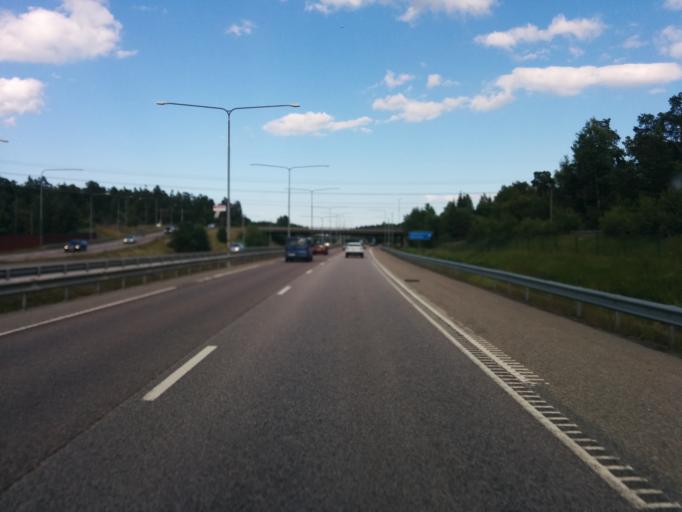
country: SE
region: Stockholm
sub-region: Nacka Kommun
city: Fisksatra
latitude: 59.3153
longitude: 18.2504
